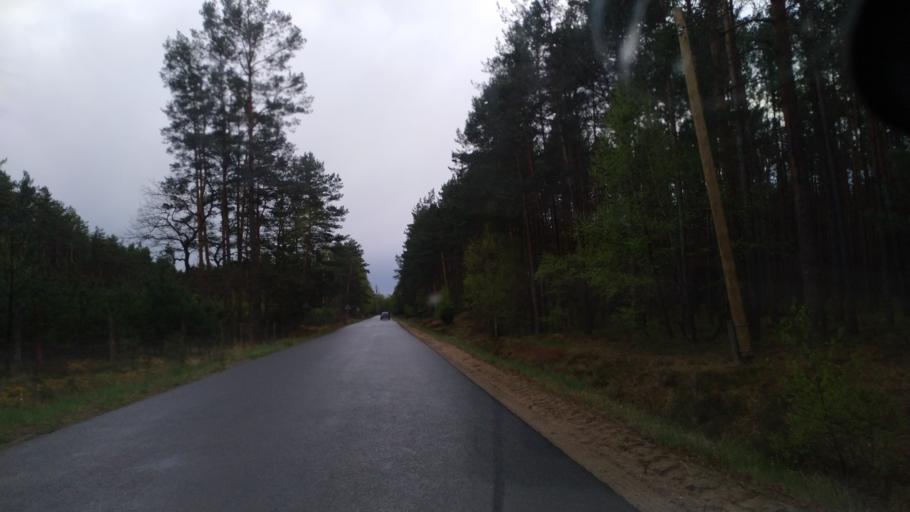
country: PL
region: Pomeranian Voivodeship
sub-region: Powiat starogardzki
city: Osiek
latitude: 53.6494
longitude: 18.4912
